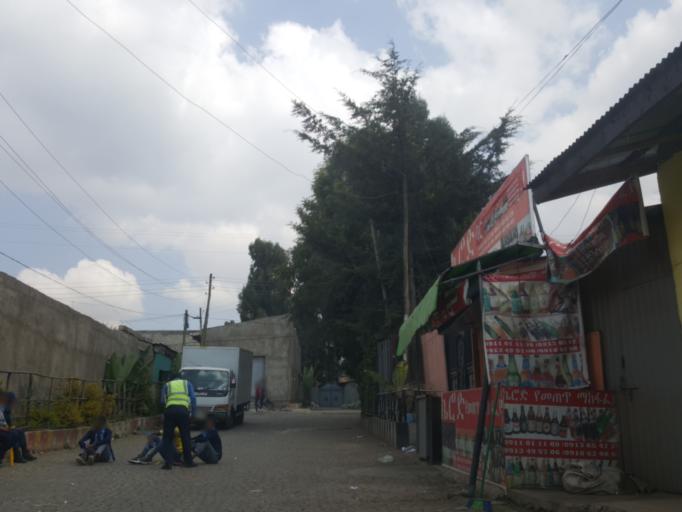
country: ET
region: Adis Abeba
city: Addis Ababa
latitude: 9.0623
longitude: 38.7211
